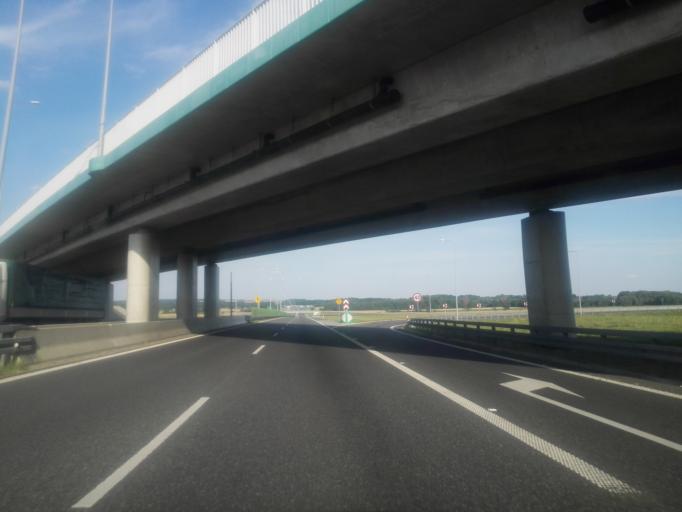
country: PL
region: Lower Silesian Voivodeship
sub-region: Powiat olesnicki
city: Sycow
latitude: 51.2955
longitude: 17.6795
